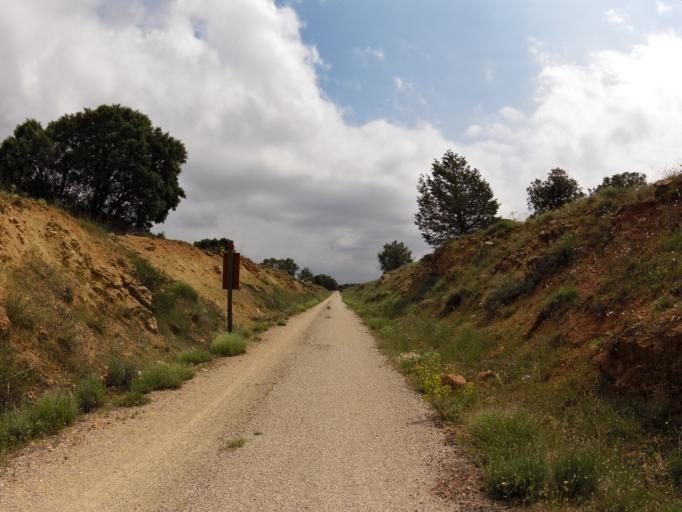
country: ES
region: Castille-La Mancha
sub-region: Provincia de Albacete
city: Robledo
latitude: 38.7654
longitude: -2.4582
